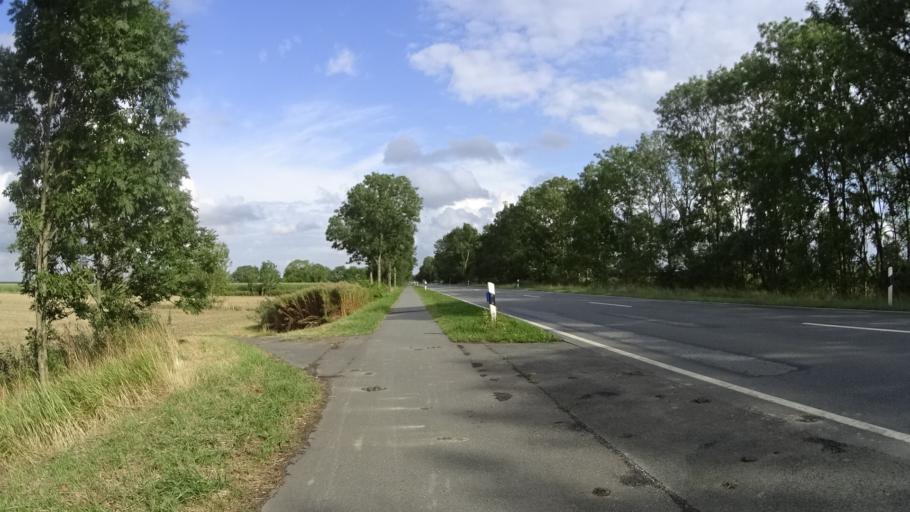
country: DE
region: Lower Saxony
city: Varel
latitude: 53.3920
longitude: 8.1851
